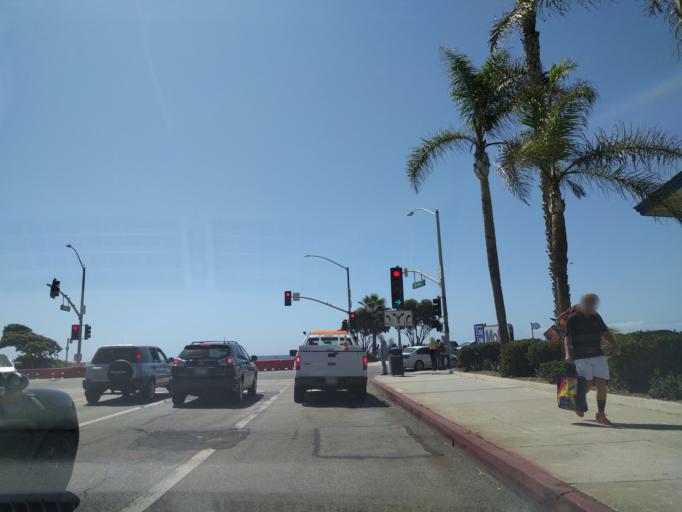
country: US
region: California
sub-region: Orange County
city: Laguna Beach
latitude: 33.5431
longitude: -117.7851
